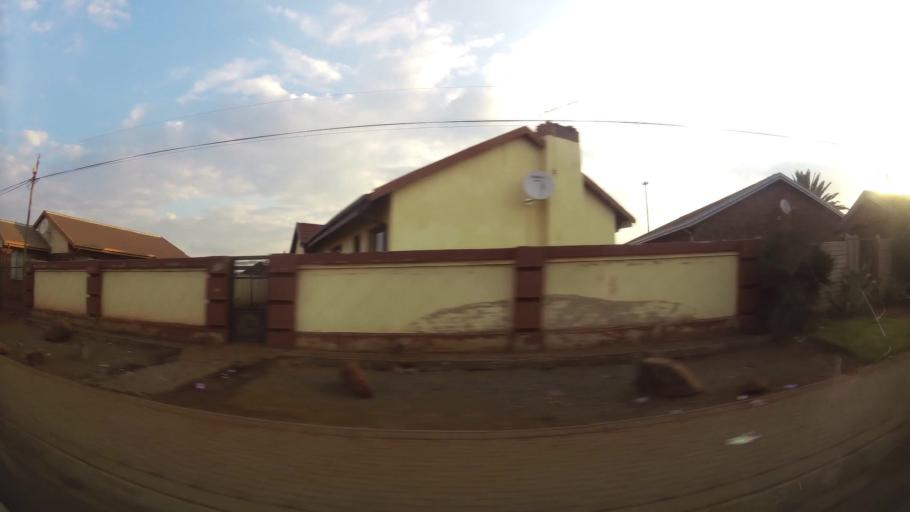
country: ZA
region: Gauteng
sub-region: City of Johannesburg Metropolitan Municipality
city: Orange Farm
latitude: -26.5639
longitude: 27.8617
